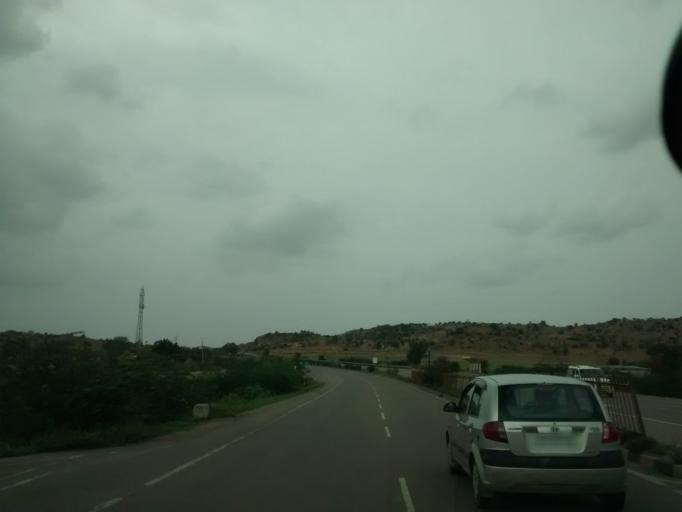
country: IN
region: Andhra Pradesh
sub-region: Kurnool
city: Ramapuram
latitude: 15.1801
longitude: 77.6879
